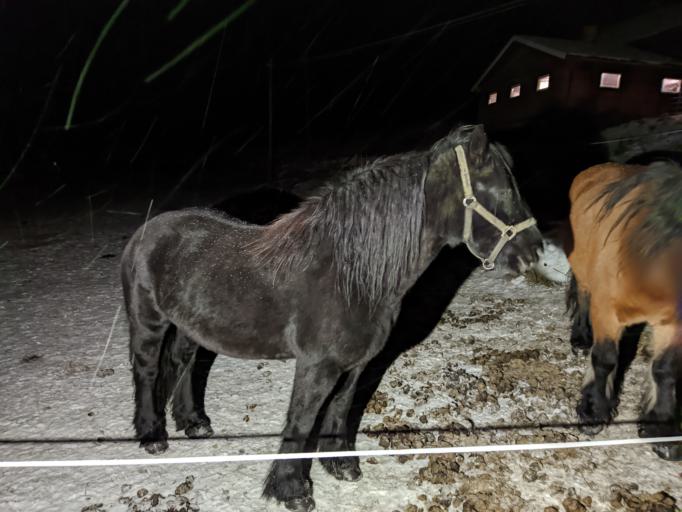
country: NO
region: Oppland
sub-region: Sel
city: Otta
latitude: 61.6832
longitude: 9.5207
